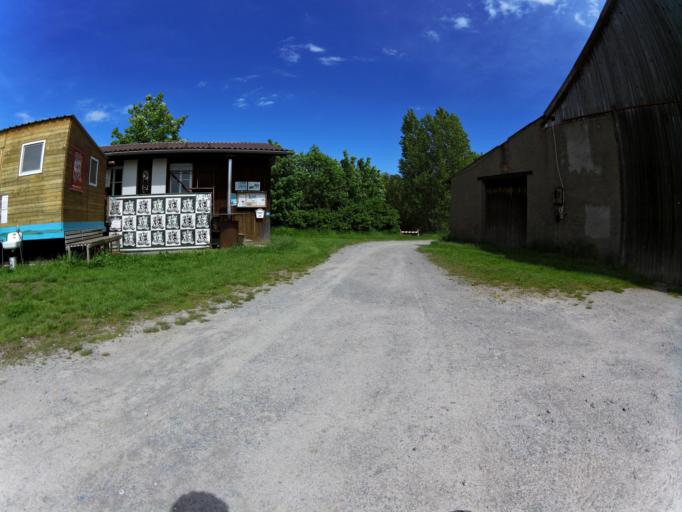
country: DE
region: Bavaria
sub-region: Regierungsbezirk Unterfranken
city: Nordheim
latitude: 49.8607
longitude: 10.1824
